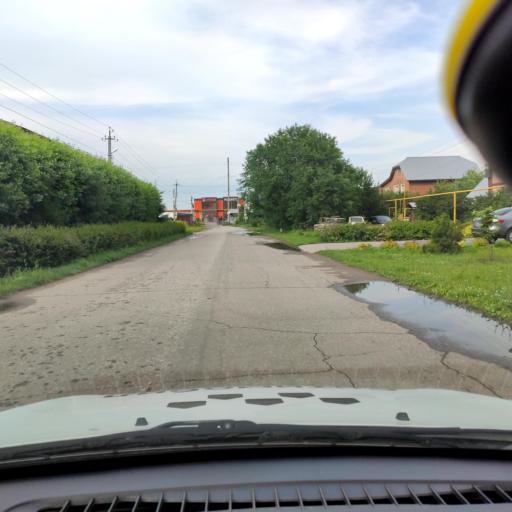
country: RU
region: Samara
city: Podstepki
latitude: 53.5737
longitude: 49.0752
